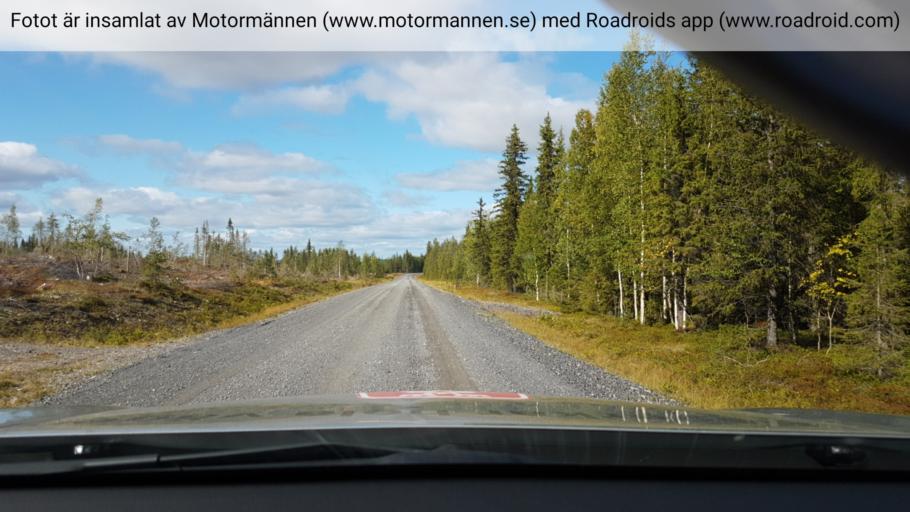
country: SE
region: Vaesterbotten
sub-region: Mala Kommun
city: Mala
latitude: 65.3324
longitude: 18.7640
